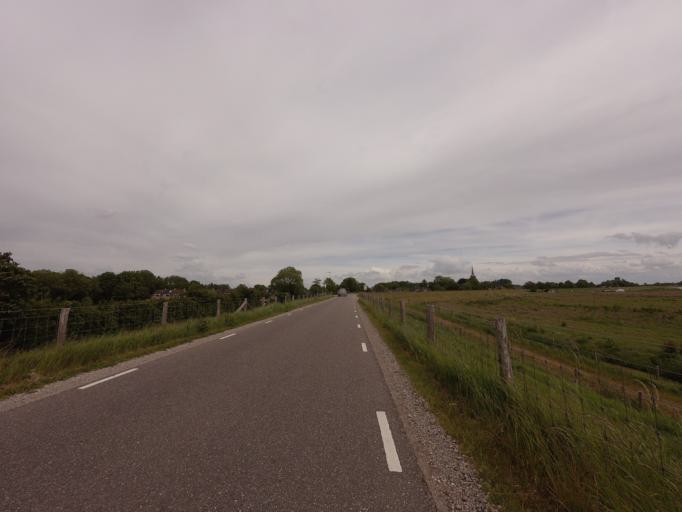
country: NL
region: North Holland
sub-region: Gemeente Hoorn
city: Hoorn
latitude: 52.6358
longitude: 5.1160
